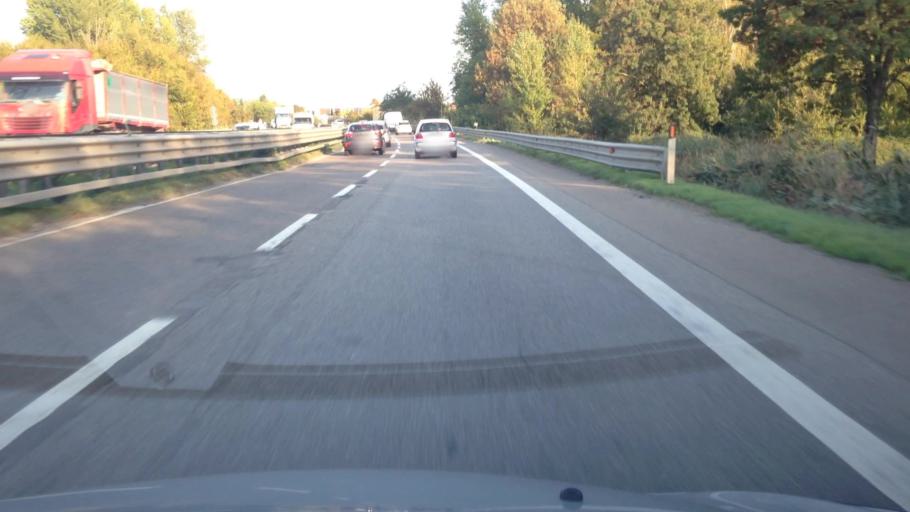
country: IT
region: Emilia-Romagna
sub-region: Provincia di Modena
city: Villanova
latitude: 44.6637
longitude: 10.8928
